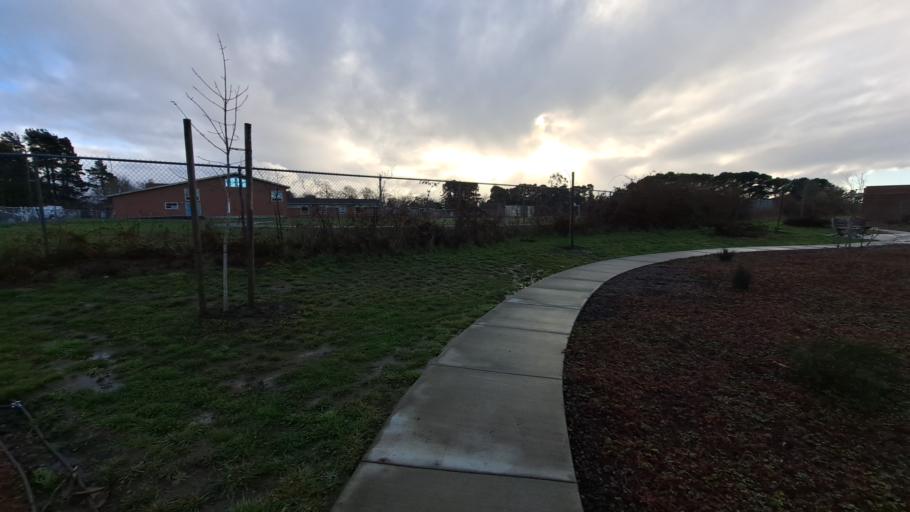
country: US
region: California
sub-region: Humboldt County
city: Fortuna
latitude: 40.5812
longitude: -124.1319
